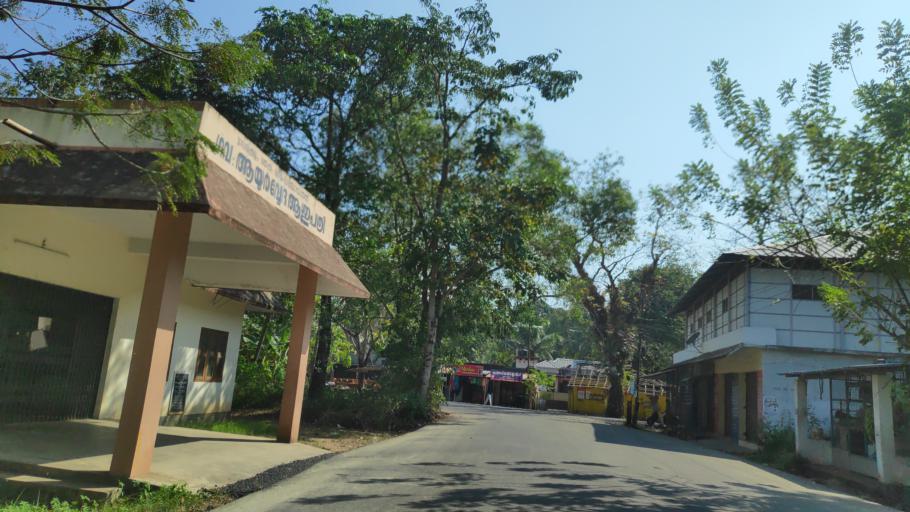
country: IN
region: Kerala
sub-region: Alappuzha
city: Alleppey
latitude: 9.5707
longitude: 76.3170
